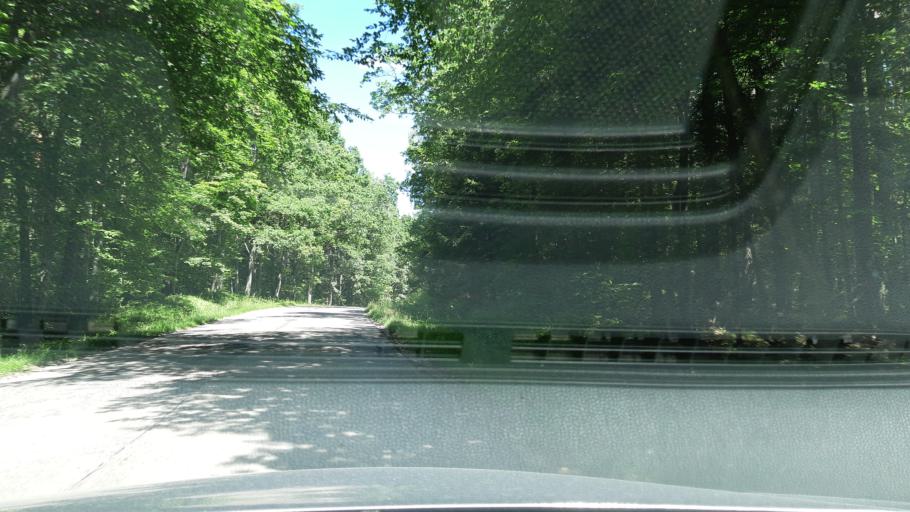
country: PL
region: Warmian-Masurian Voivodeship
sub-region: Powiat mragowski
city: Mikolajki
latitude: 53.7624
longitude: 21.5022
